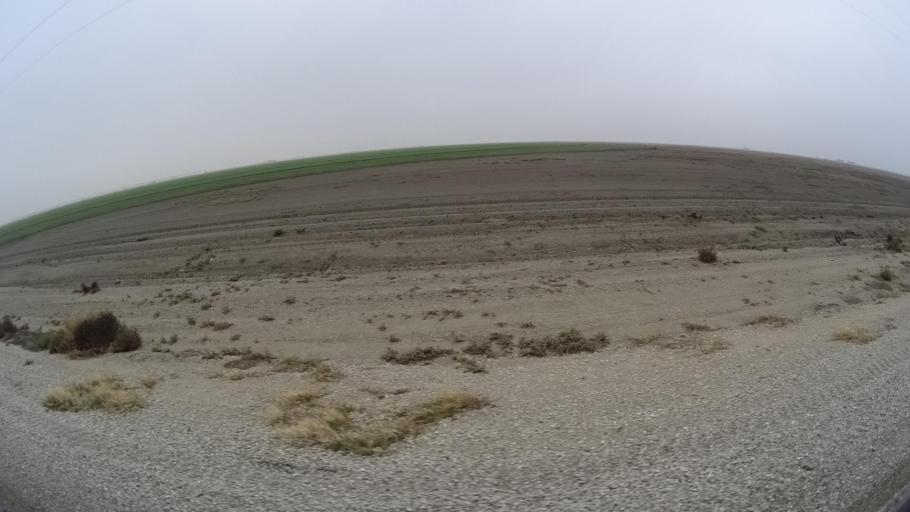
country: US
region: California
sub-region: Kern County
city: Greenfield
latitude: 35.1624
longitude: -119.1990
